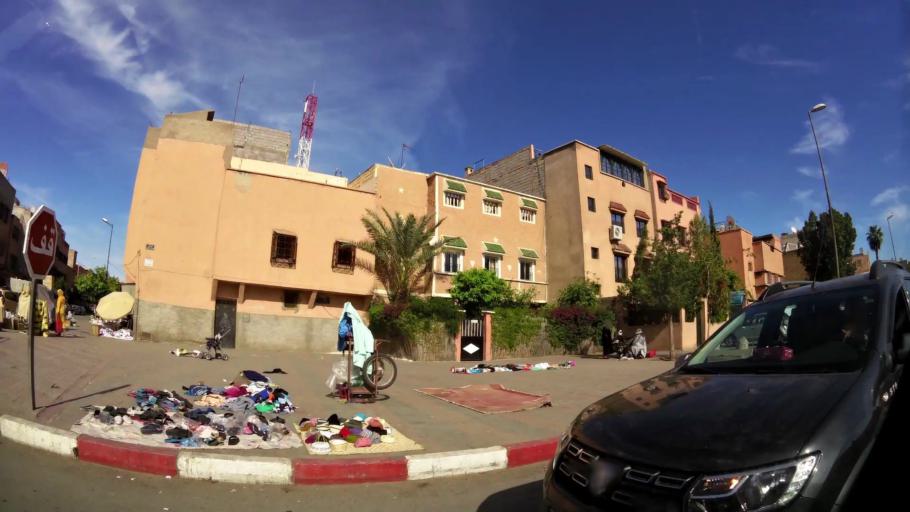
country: MA
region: Marrakech-Tensift-Al Haouz
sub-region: Marrakech
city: Marrakesh
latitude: 31.6091
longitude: -7.9614
